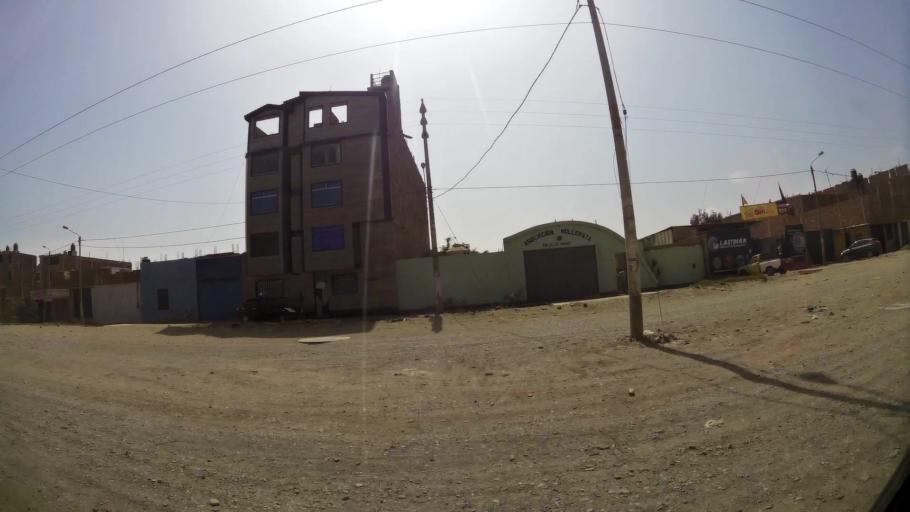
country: PE
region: La Libertad
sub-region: Provincia de Trujillo
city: Buenos Aires
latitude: -8.1325
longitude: -79.0515
